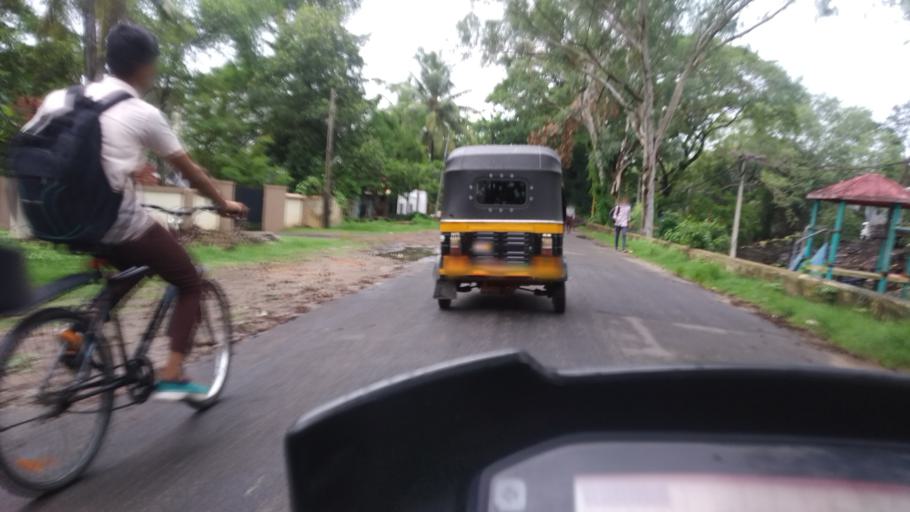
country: IN
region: Kerala
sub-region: Alappuzha
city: Alleppey
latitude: 9.5001
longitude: 76.3271
